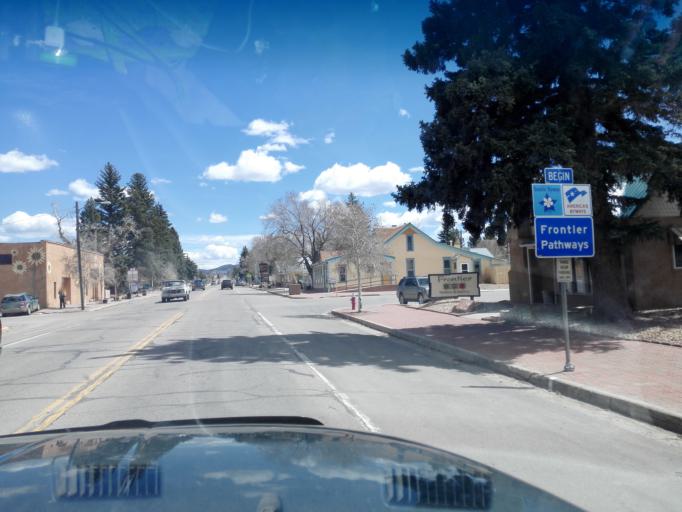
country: US
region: Colorado
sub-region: Custer County
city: Westcliffe
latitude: 38.1360
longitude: -105.4667
